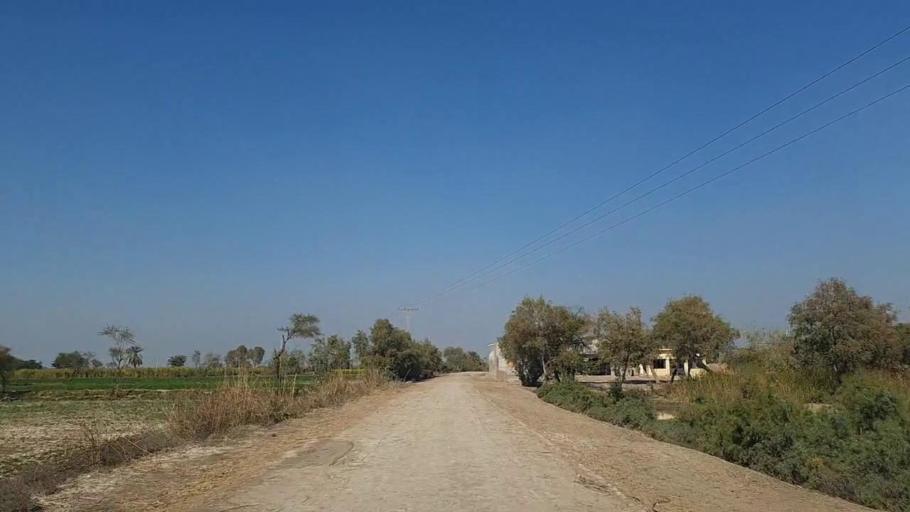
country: PK
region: Sindh
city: Bandhi
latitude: 26.5465
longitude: 68.3270
